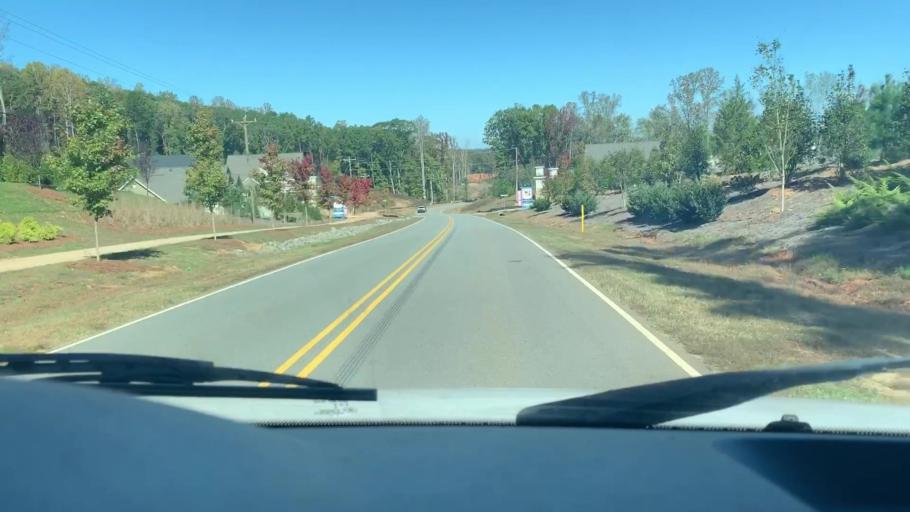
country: US
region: North Carolina
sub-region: Gaston County
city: Davidson
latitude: 35.4609
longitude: -80.8212
